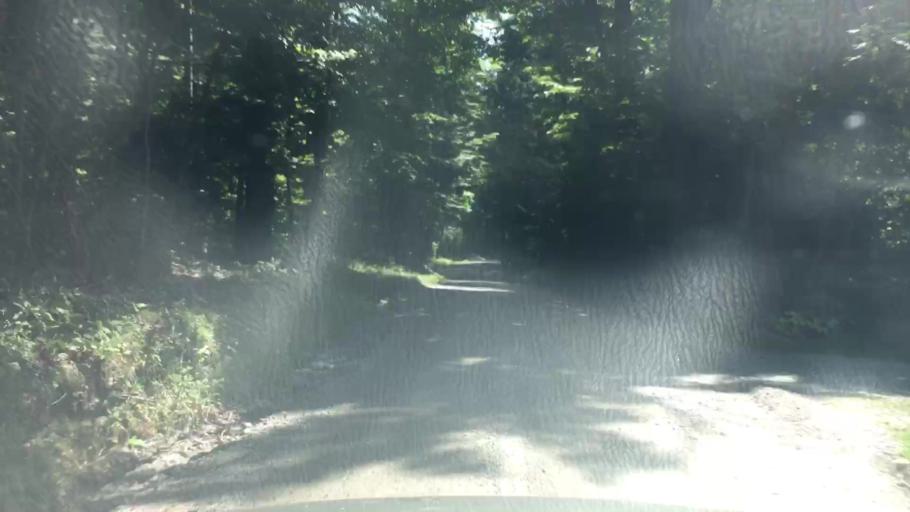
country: US
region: Vermont
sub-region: Windham County
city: West Brattleboro
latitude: 42.8015
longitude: -72.6442
